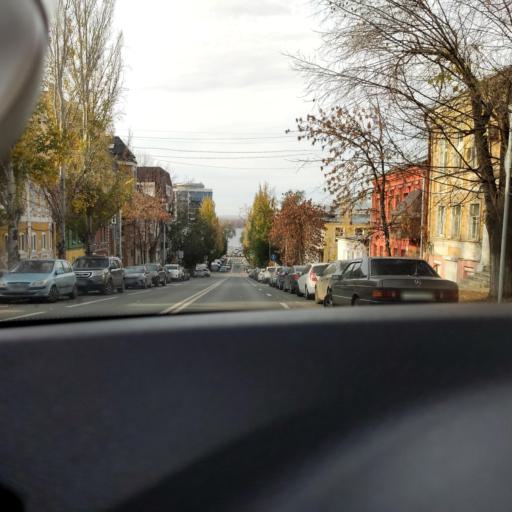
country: RU
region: Samara
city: Rozhdestveno
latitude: 53.1862
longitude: 50.0851
